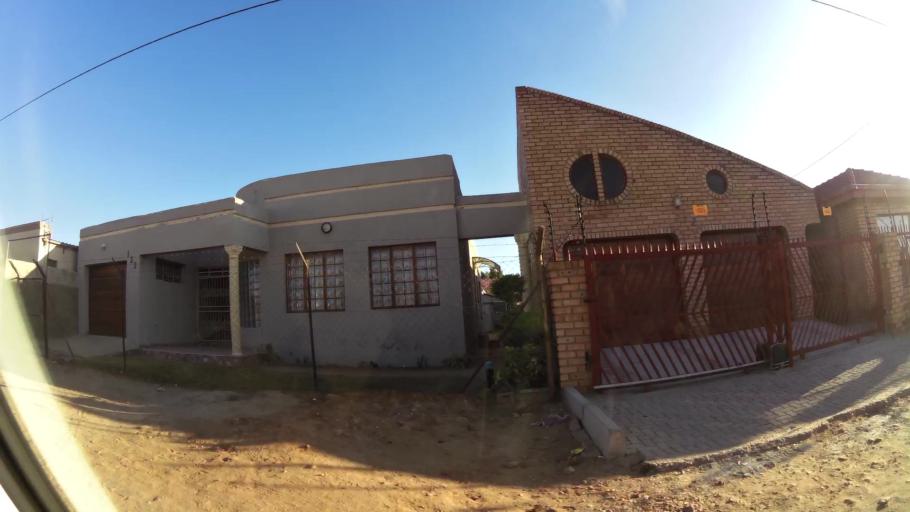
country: ZA
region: Limpopo
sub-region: Capricorn District Municipality
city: Polokwane
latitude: -23.8464
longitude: 29.3550
